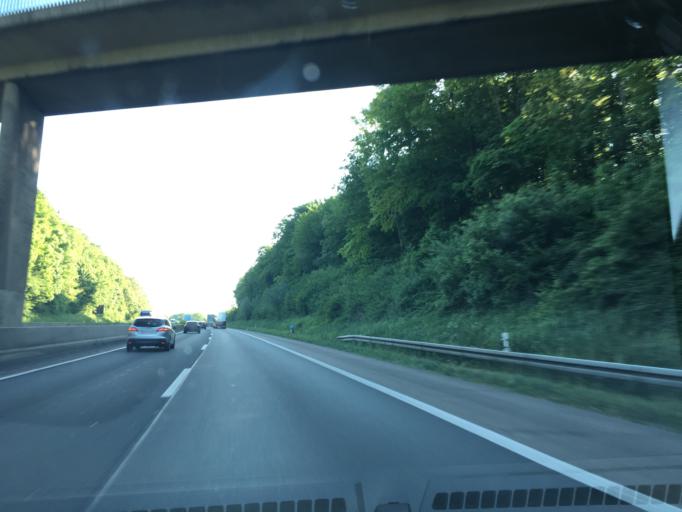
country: DE
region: Lower Saxony
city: Hasbergen
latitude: 52.2501
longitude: 7.9120
